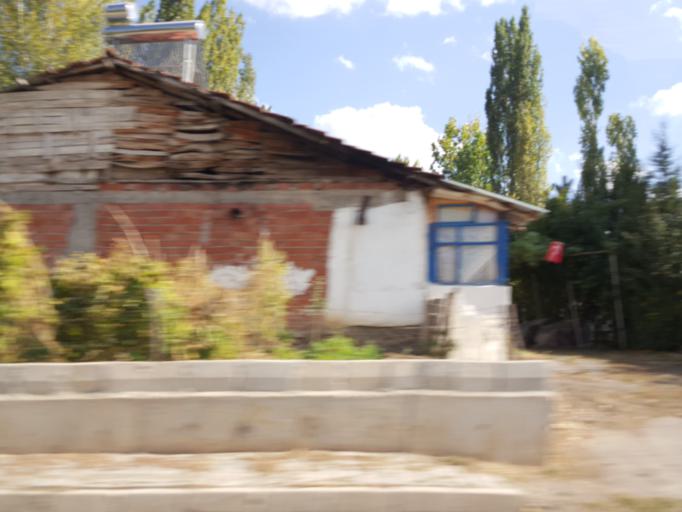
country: TR
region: Tokat
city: Sulusaray
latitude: 39.9874
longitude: 36.0776
